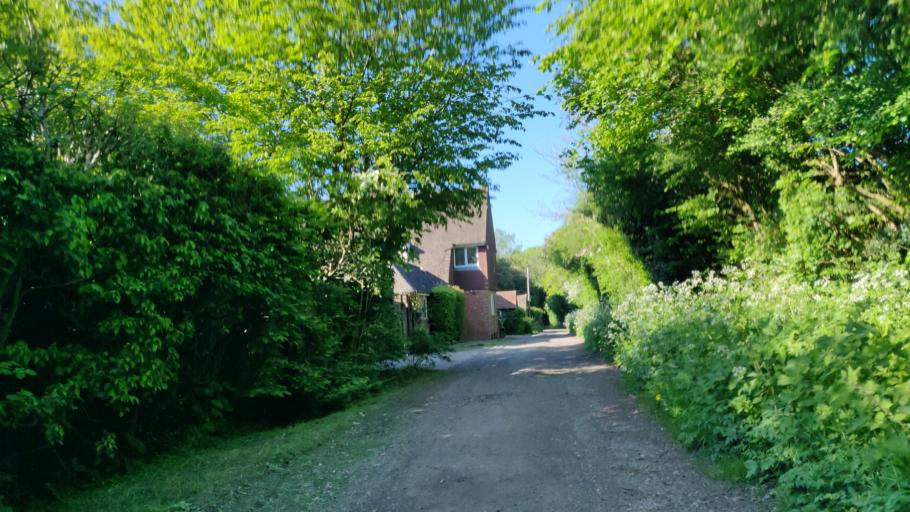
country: GB
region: England
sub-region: West Sussex
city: Southwater
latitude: 51.0448
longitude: -0.3880
